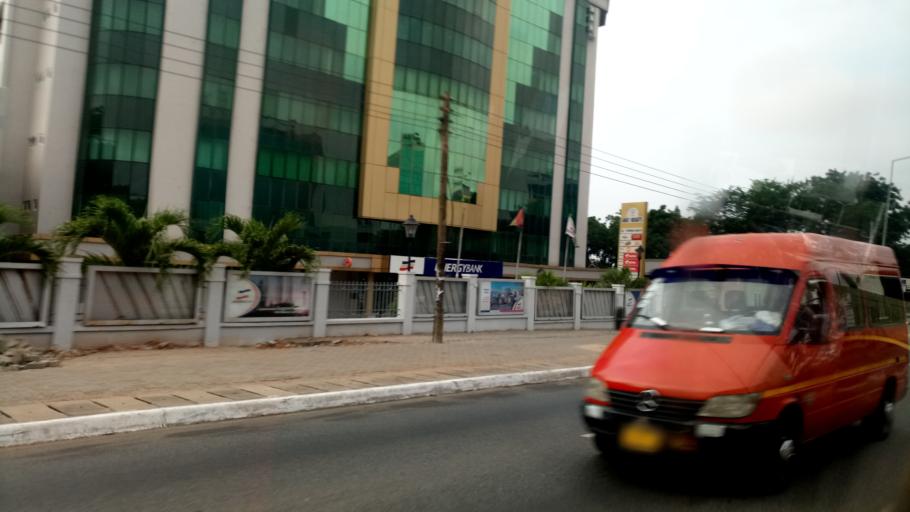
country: GH
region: Greater Accra
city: Accra
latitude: 5.5660
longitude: -0.1937
